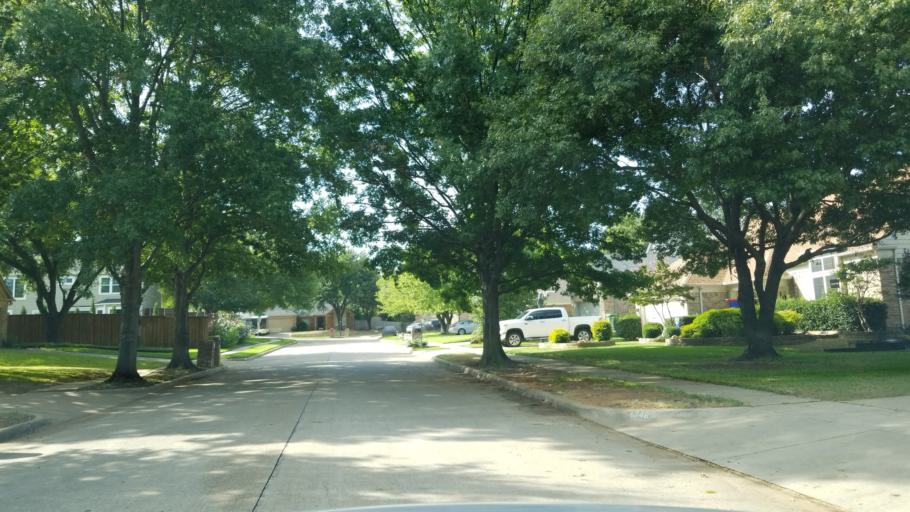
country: US
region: Texas
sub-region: Tarrant County
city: Grapevine
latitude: 32.8910
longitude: -97.0861
